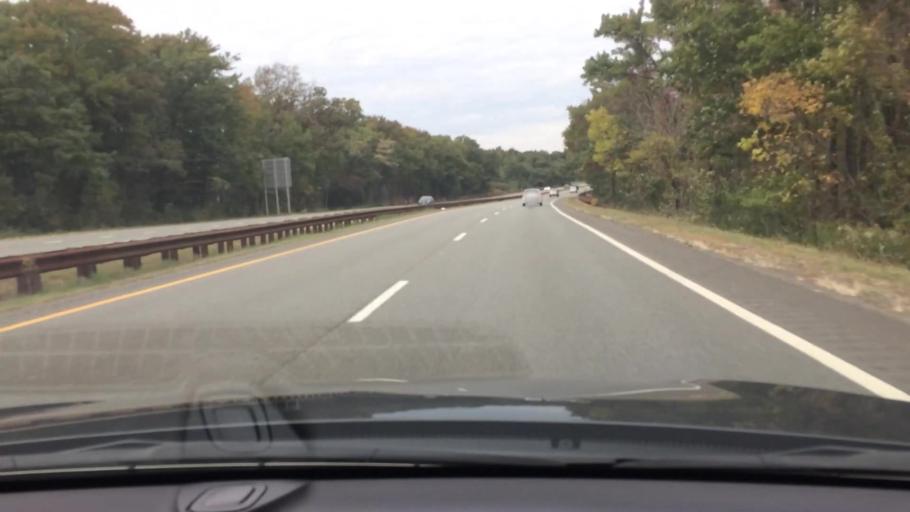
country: US
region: New Jersey
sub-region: Bergen County
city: Englewood Cliffs
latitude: 40.8762
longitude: -73.9502
